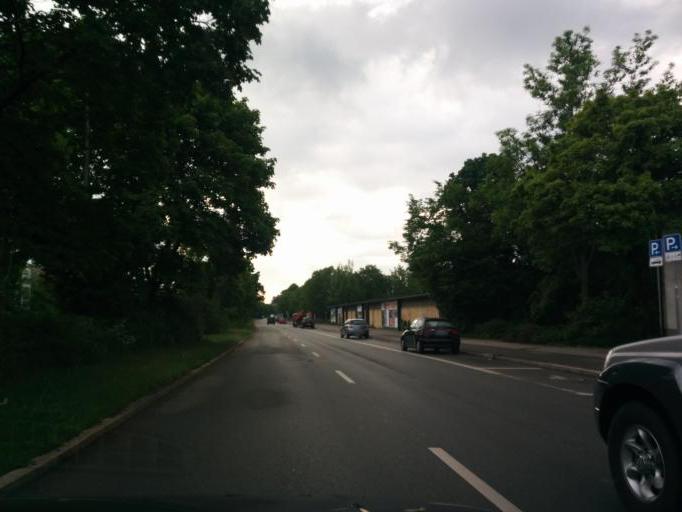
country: DE
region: Bavaria
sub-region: Upper Bavaria
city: Bogenhausen
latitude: 48.1183
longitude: 11.6332
